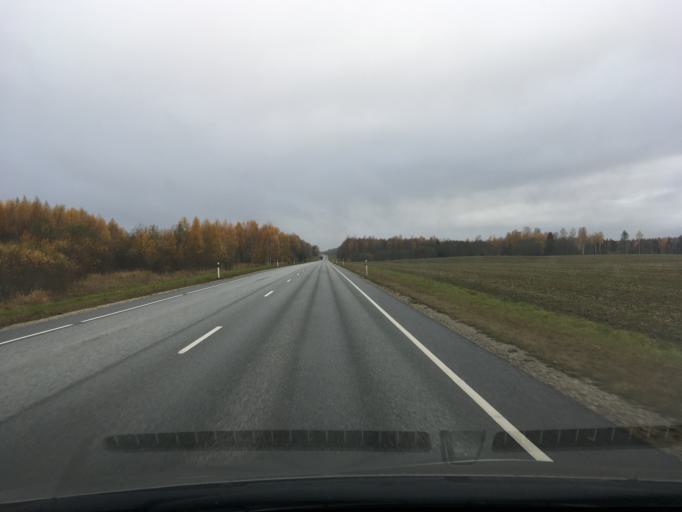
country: EE
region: Tartu
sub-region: Noo vald
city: Noo
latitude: 58.2899
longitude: 26.5637
